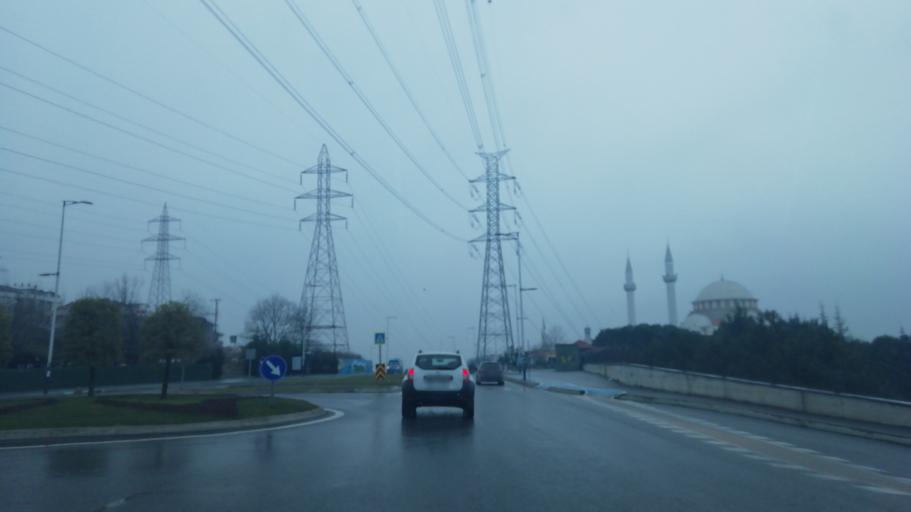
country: TR
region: Sakarya
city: Adapazari
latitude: 40.7457
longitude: 30.3452
